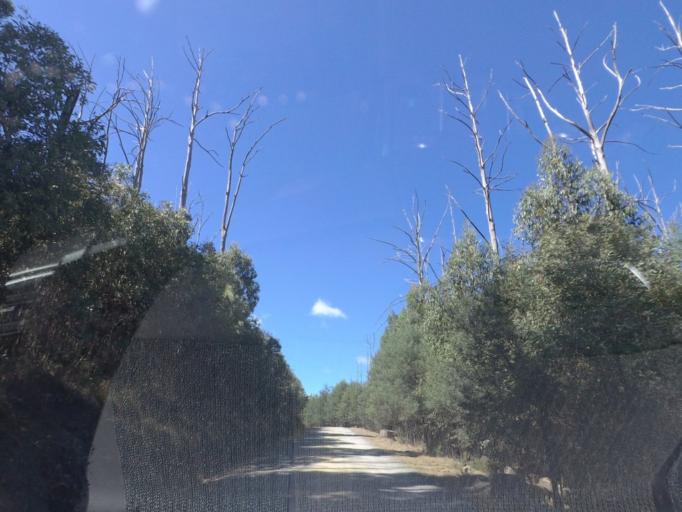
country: AU
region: Victoria
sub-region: Yarra Ranges
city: Millgrove
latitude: -37.5436
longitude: 145.7499
